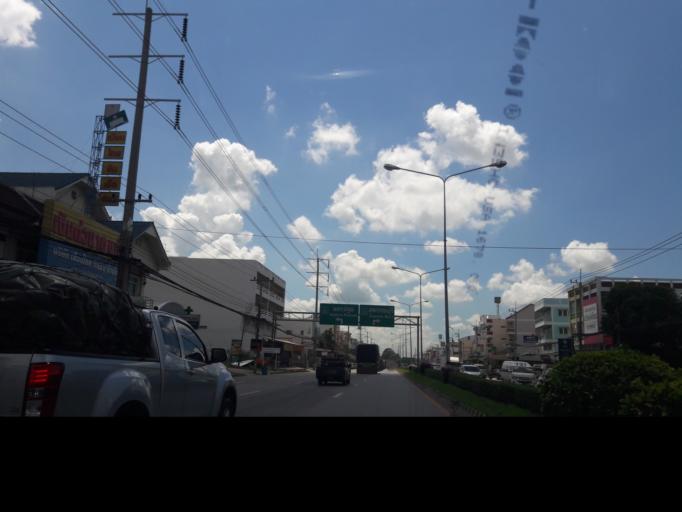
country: TH
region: Nakhon Pathom
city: Kamphaeng Saen
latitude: 14.0058
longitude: 99.9944
